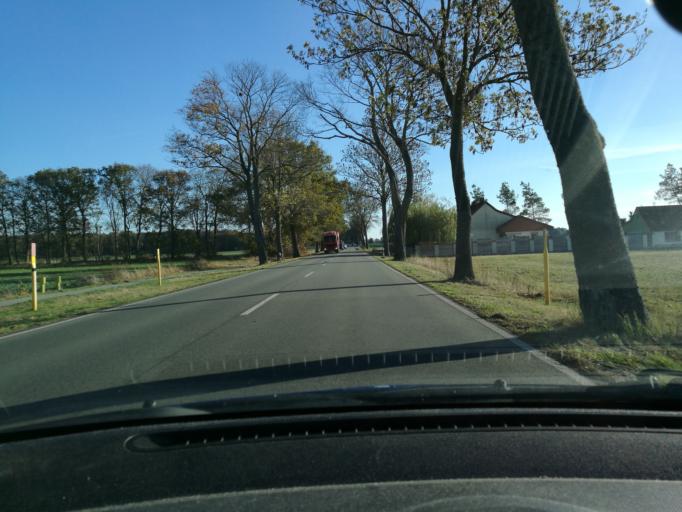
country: DE
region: Brandenburg
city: Perleberg
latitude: 53.1155
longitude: 11.8147
